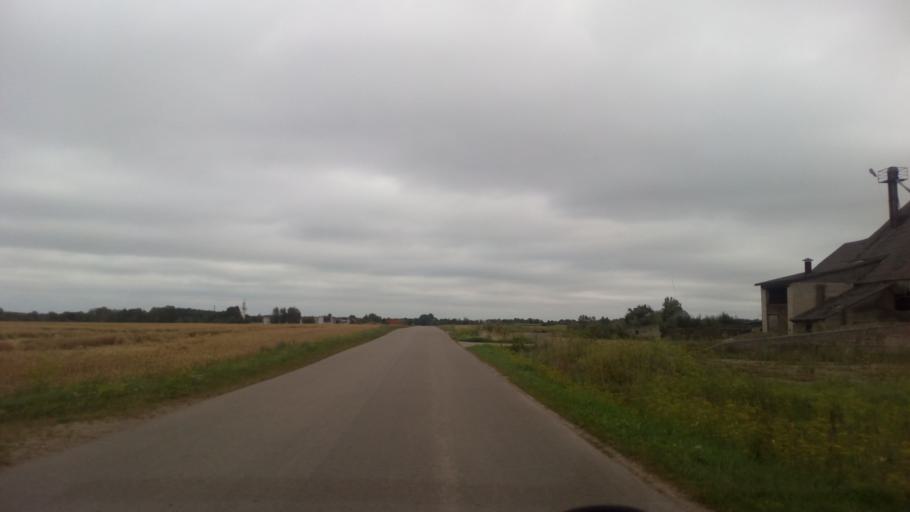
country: LV
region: Rundales
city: Pilsrundale
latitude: 56.4247
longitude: 23.9928
